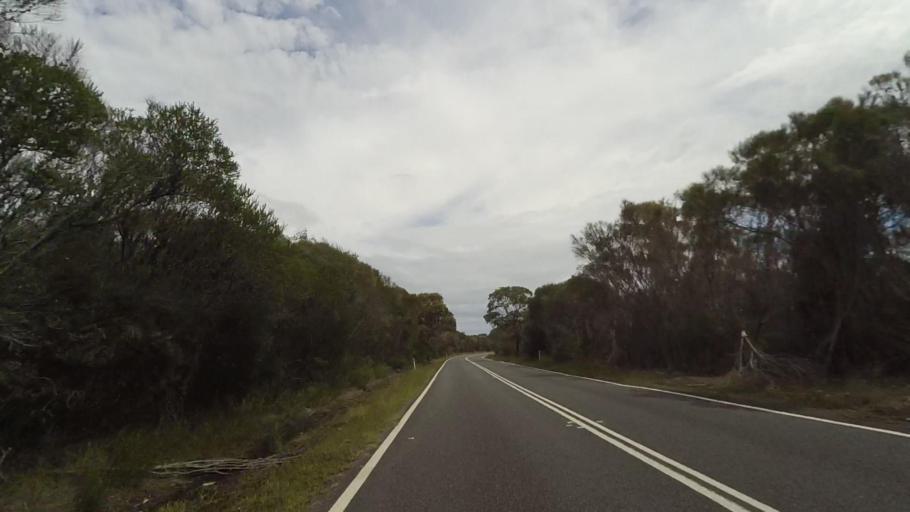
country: AU
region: New South Wales
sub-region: Sutherland Shire
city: Bundeena
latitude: -34.0929
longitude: 151.1342
